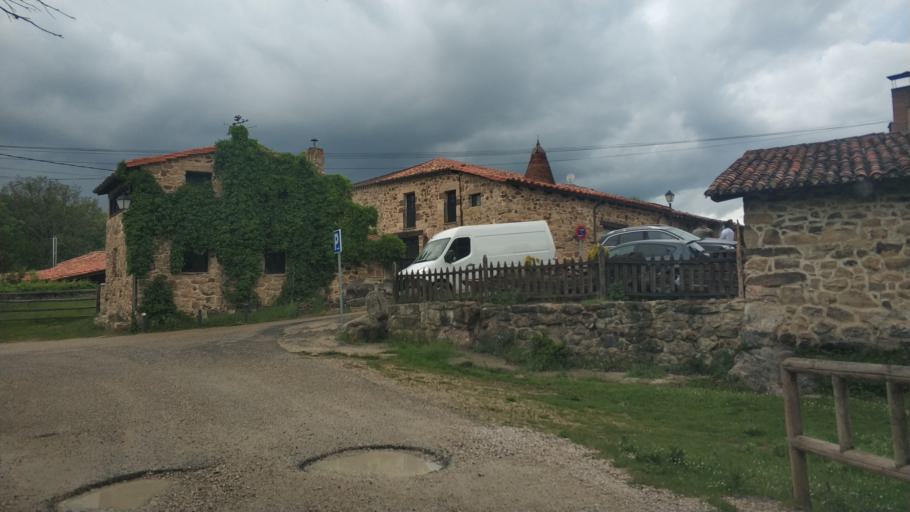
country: ES
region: Castille and Leon
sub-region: Provincia de Soria
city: Vinuesa
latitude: 41.9725
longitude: -2.7770
